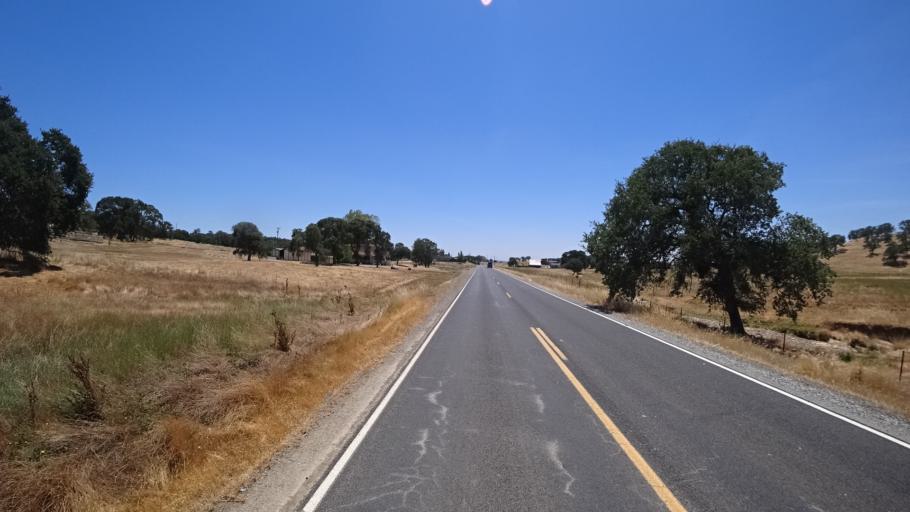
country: US
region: California
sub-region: Calaveras County
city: Rancho Calaveras
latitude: 38.1149
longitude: -120.8796
